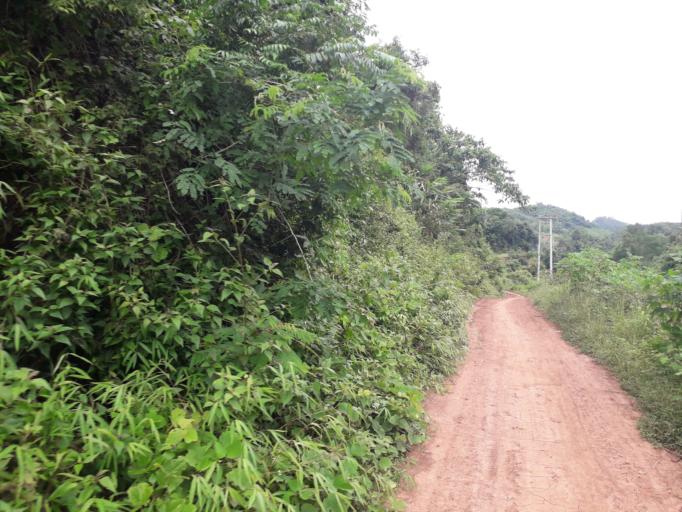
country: CN
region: Yunnan
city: Menglie
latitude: 22.2171
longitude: 101.6519
